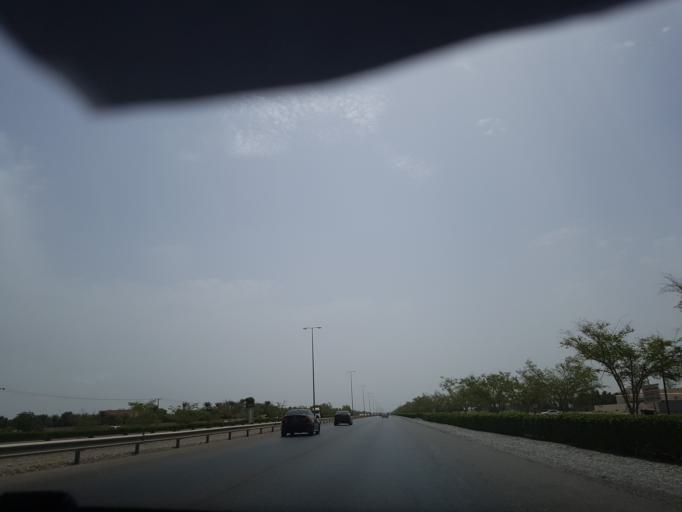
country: OM
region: Al Batinah
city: Barka'
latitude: 23.7326
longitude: 57.6914
